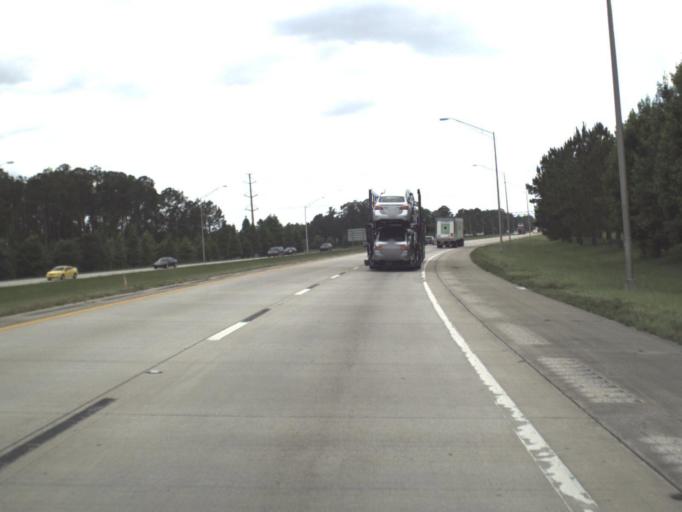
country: US
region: Florida
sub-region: Saint Johns County
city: Palm Valley
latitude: 30.1762
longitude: -81.5178
